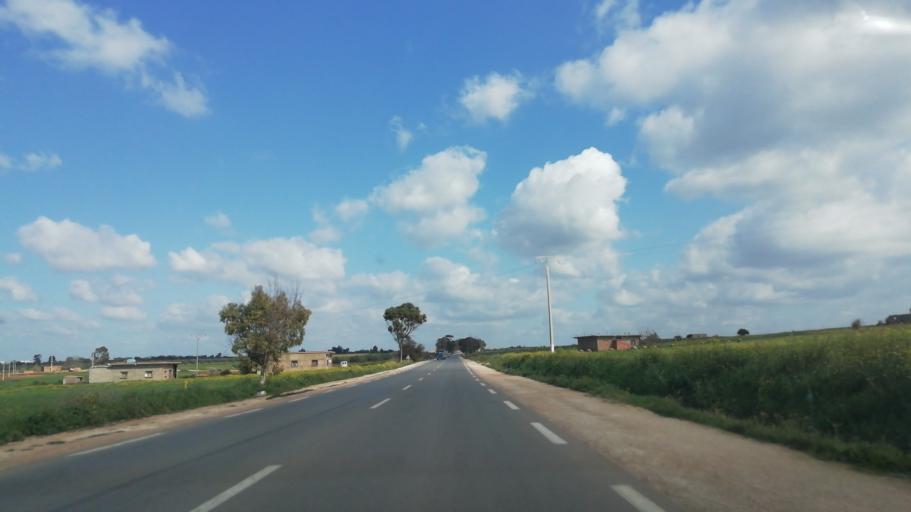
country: DZ
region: Relizane
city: Relizane
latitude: 35.7149
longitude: 0.2948
